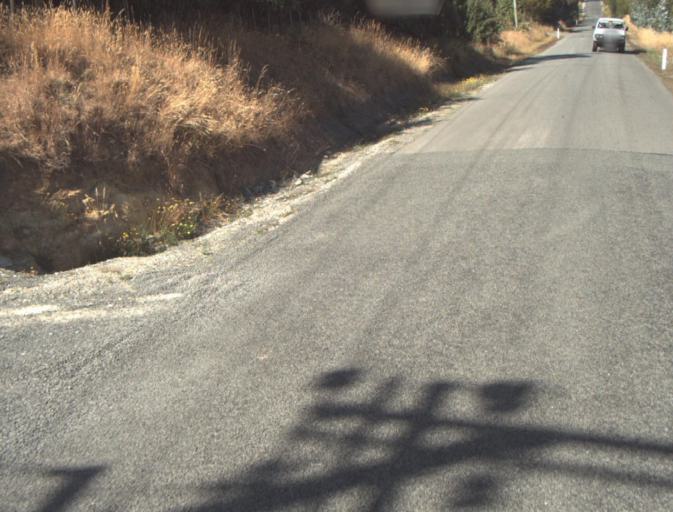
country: AU
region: Tasmania
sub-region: Launceston
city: Mayfield
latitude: -41.2344
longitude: 147.2346
